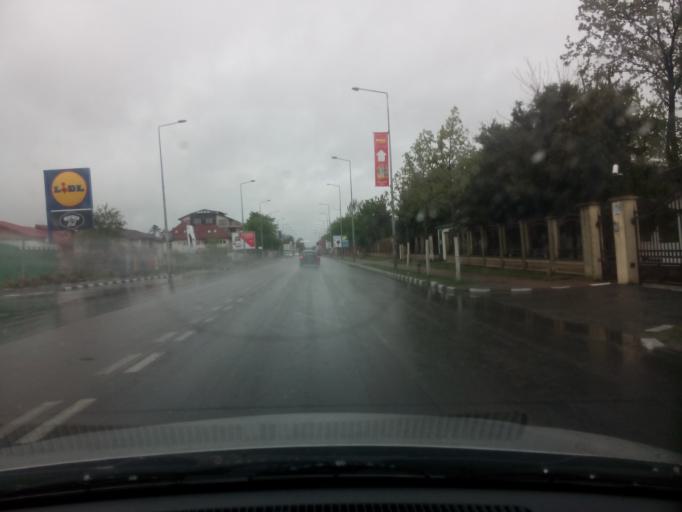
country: RO
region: Ilfov
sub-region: Comuna Tunari
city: Tunari
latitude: 44.5144
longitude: 26.1228
